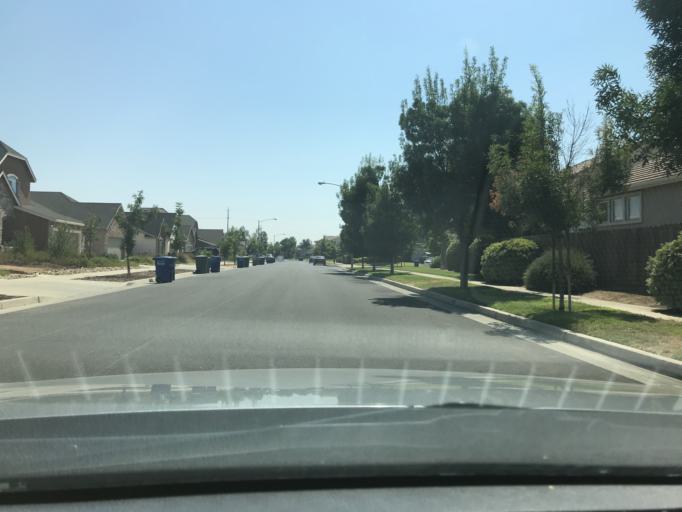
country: US
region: California
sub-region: Merced County
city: Merced
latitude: 37.3563
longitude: -120.4715
